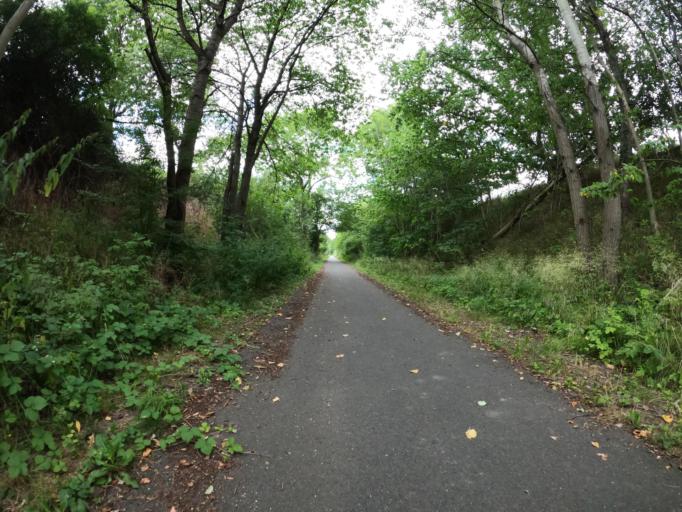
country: DE
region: Mecklenburg-Vorpommern
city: Woldegk
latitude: 53.3636
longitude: 13.5899
